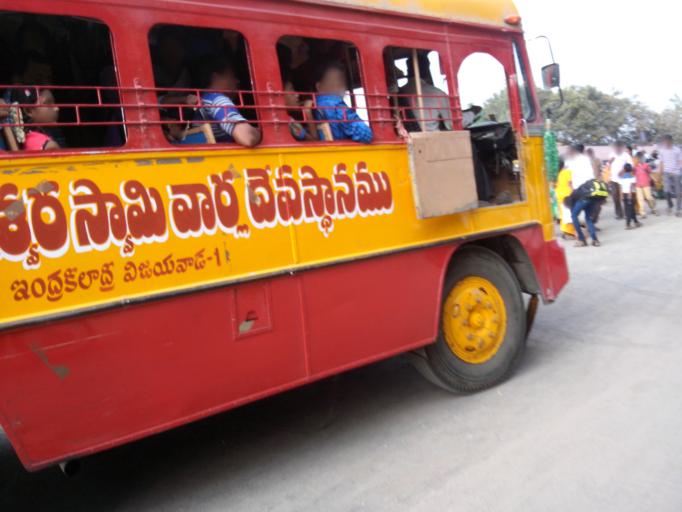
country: IN
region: Andhra Pradesh
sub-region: Krishna
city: Vijayawada
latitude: 16.5127
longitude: 80.6047
